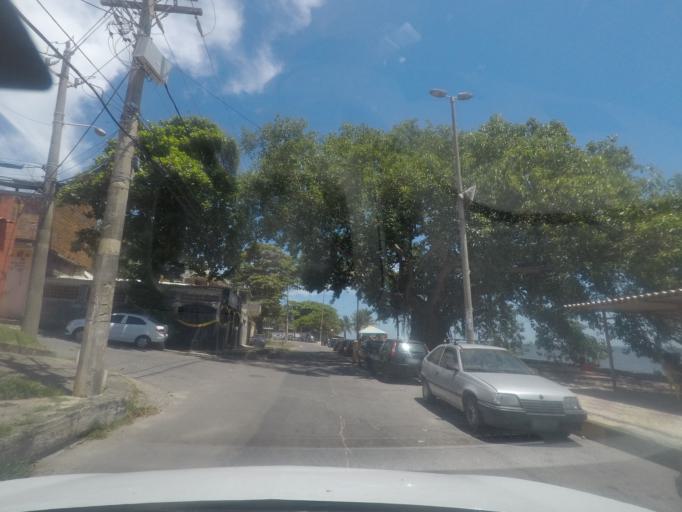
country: BR
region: Rio de Janeiro
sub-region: Itaguai
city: Itaguai
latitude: -22.9883
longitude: -43.6913
